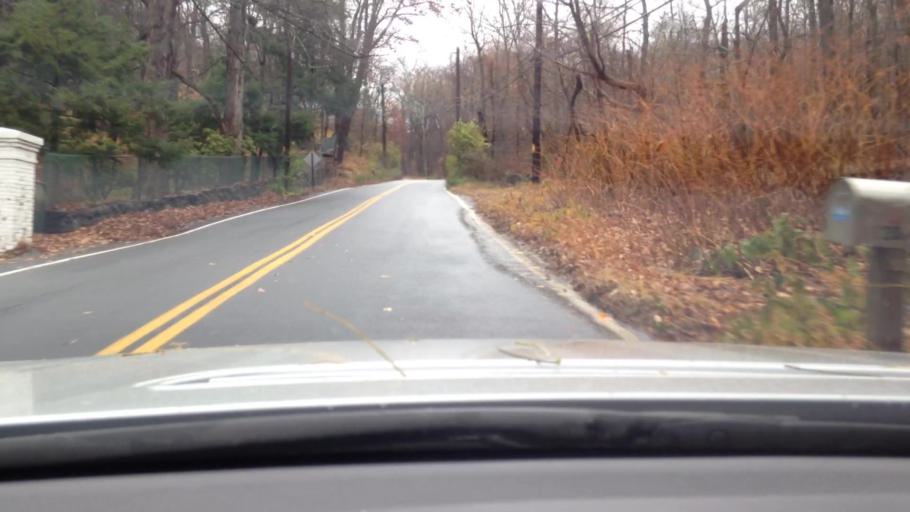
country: US
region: New York
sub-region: Westchester County
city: Croton-on-Hudson
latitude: 41.2307
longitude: -73.8847
